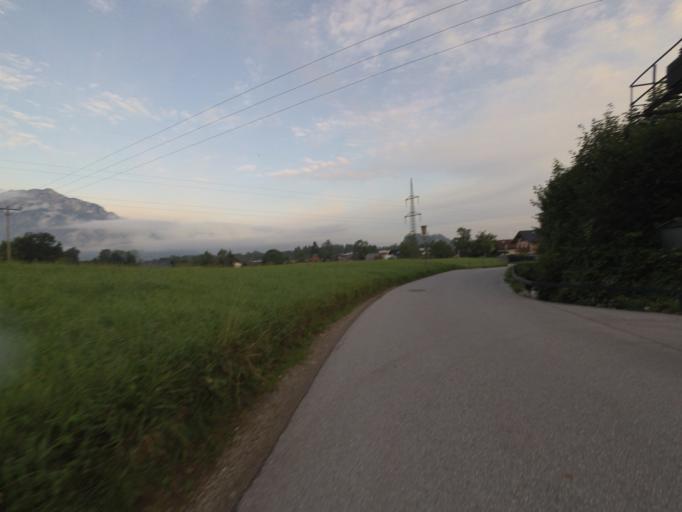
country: AT
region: Salzburg
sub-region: Politischer Bezirk Salzburg-Umgebung
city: Elsbethen
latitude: 47.7458
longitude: 13.0889
